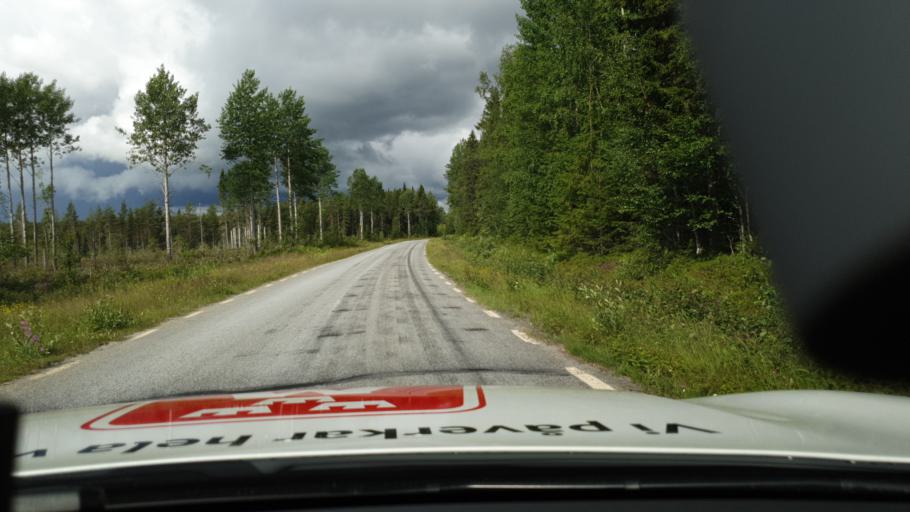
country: SE
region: Norrbotten
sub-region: Pitea Kommun
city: Rosvik
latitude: 65.4208
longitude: 21.8136
